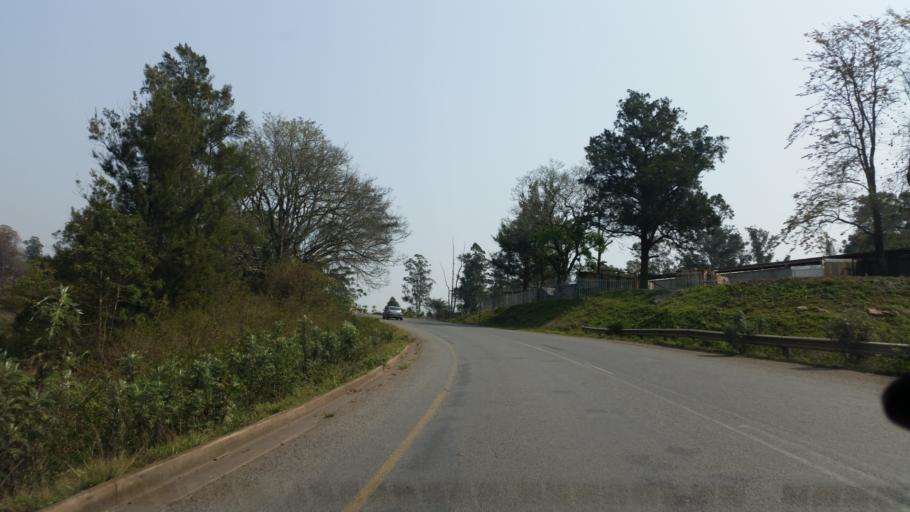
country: ZA
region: KwaZulu-Natal
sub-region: eThekwini Metropolitan Municipality
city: Mpumalanga
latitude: -29.7431
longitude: 30.6639
